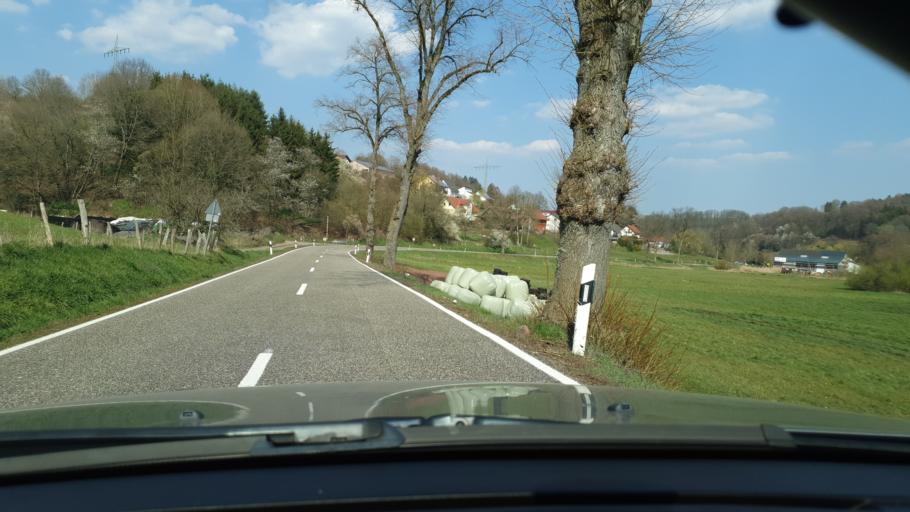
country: DE
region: Rheinland-Pfalz
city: Battweiler
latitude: 49.2940
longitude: 7.4534
